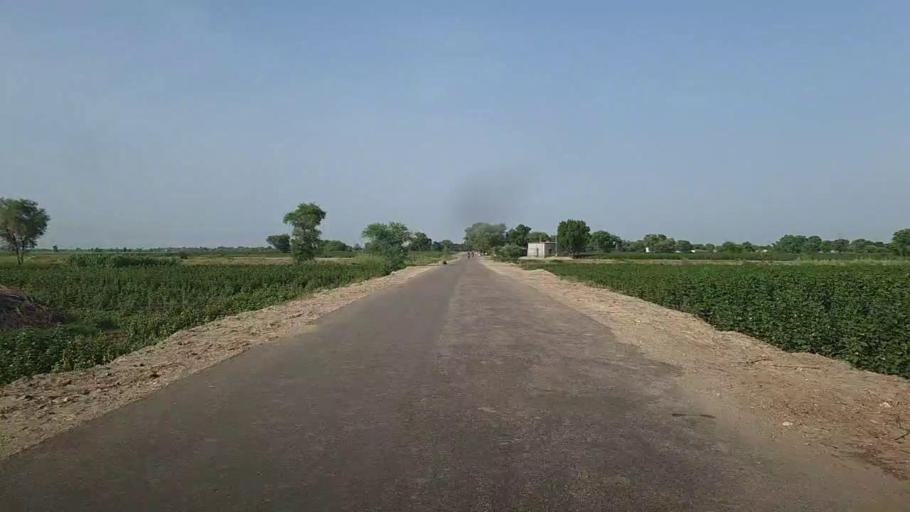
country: PK
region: Sindh
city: Khairpur
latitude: 28.0783
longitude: 69.8320
